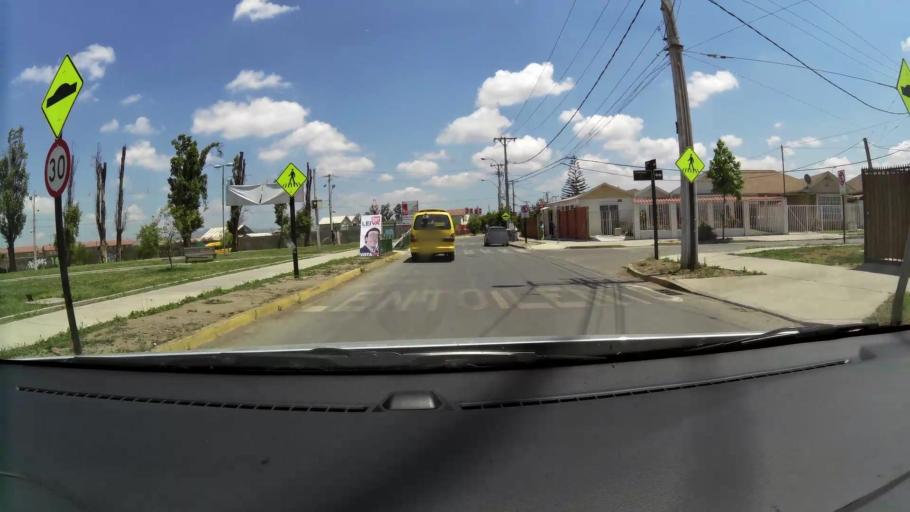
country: CL
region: Santiago Metropolitan
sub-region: Provincia de Talagante
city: Penaflor
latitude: -33.5724
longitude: -70.8033
